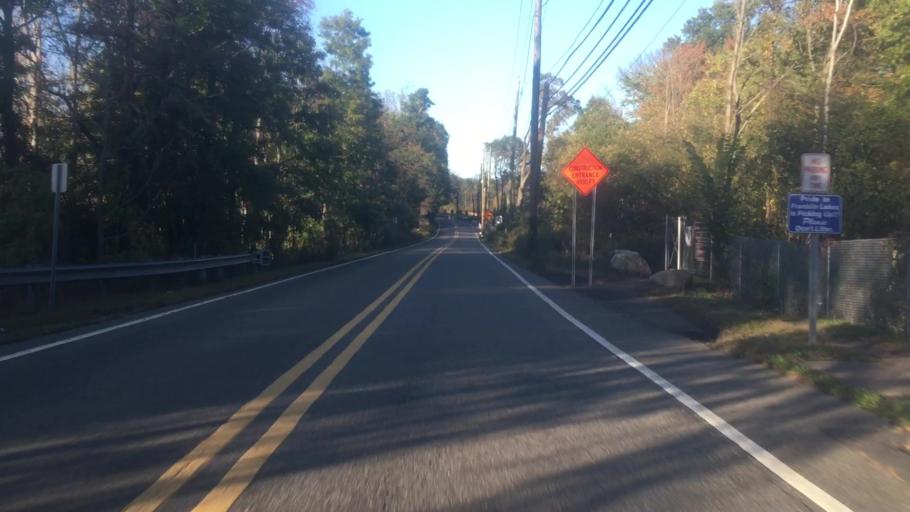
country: US
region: New Jersey
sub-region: Bergen County
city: Franklin Lakes
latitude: 40.9857
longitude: -74.2013
